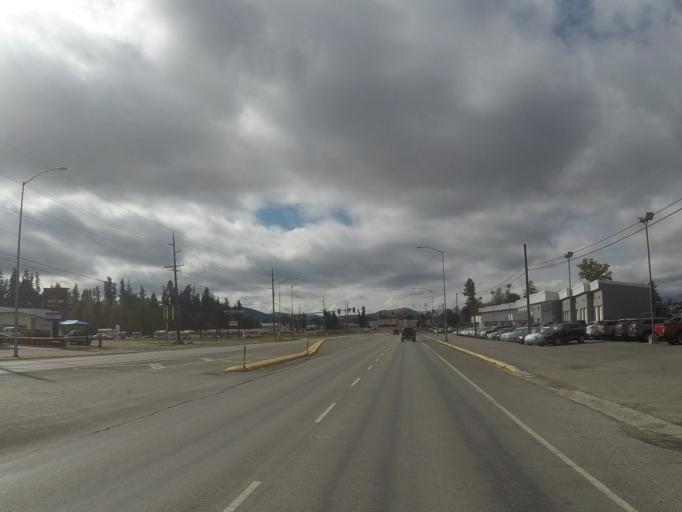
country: US
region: Montana
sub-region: Flathead County
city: Evergreen
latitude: 48.2112
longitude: -114.2865
